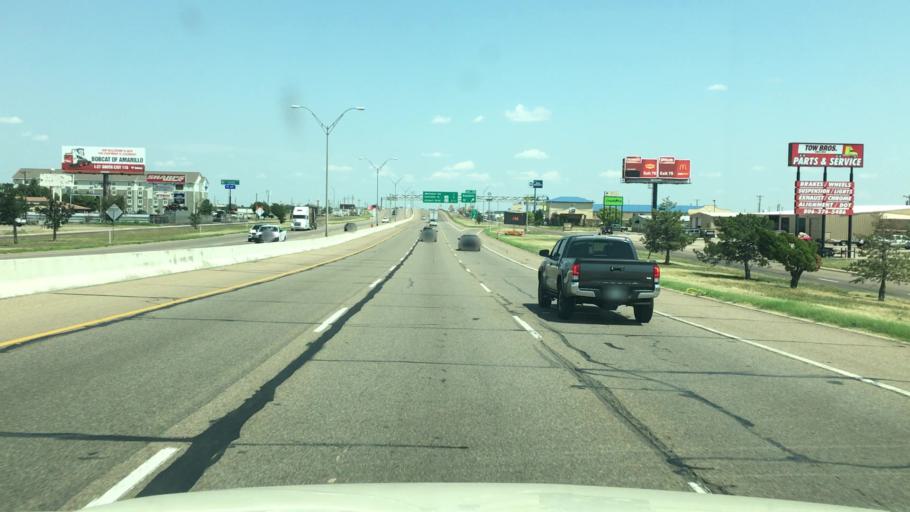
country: US
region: Texas
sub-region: Potter County
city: Amarillo
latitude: 35.1925
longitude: -101.7851
